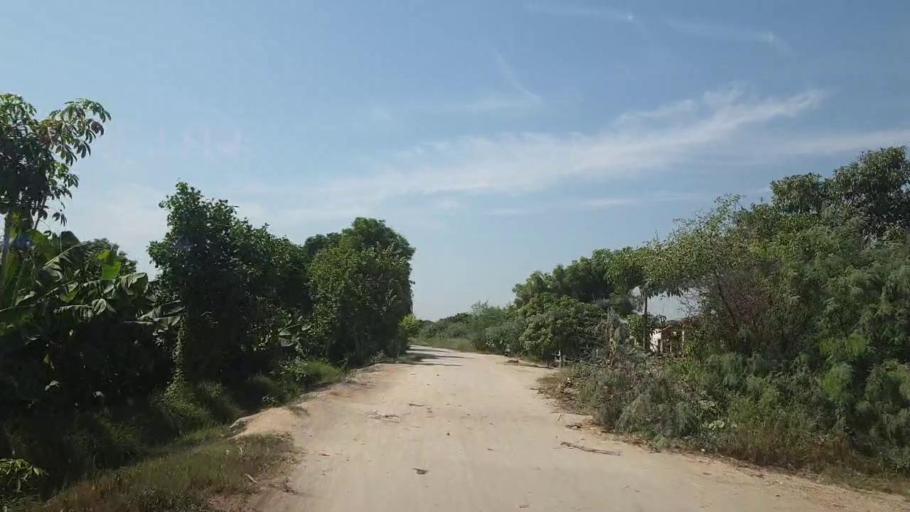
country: PK
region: Sindh
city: Tando Allahyar
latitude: 25.3991
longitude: 68.6369
